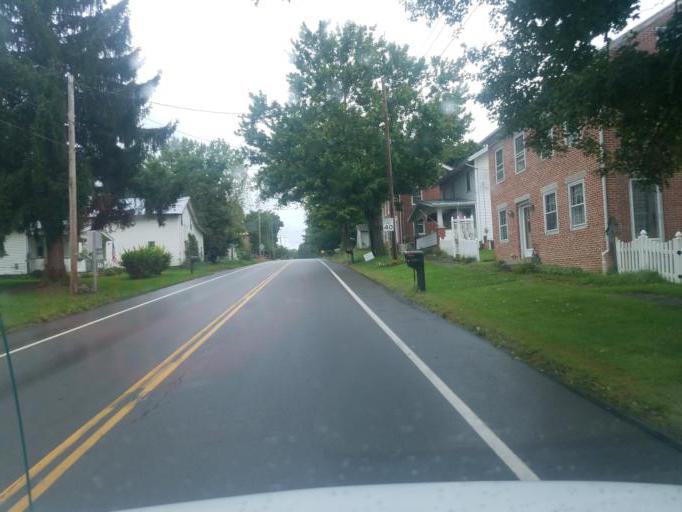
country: US
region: Ohio
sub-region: Wayne County
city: West Salem
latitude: 40.8584
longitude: -82.1564
